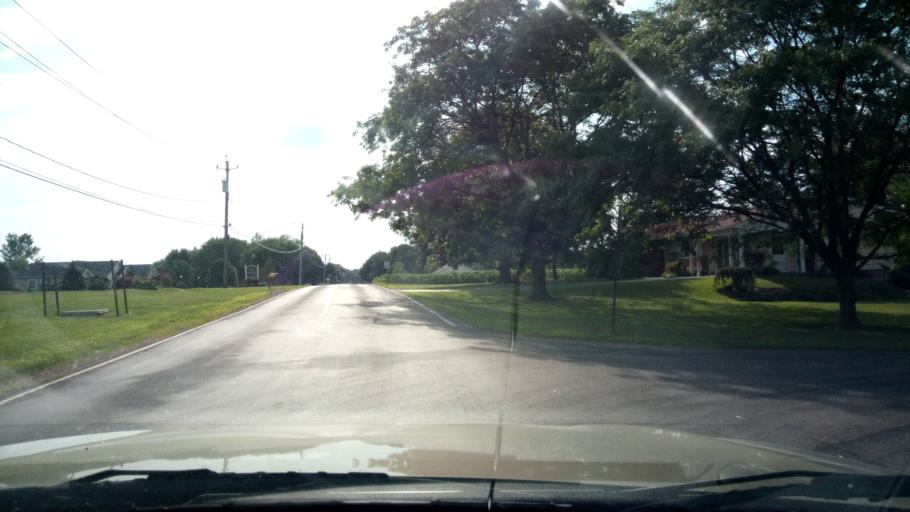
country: US
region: New York
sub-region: Wayne County
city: Lyons
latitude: 43.0465
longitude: -76.9848
